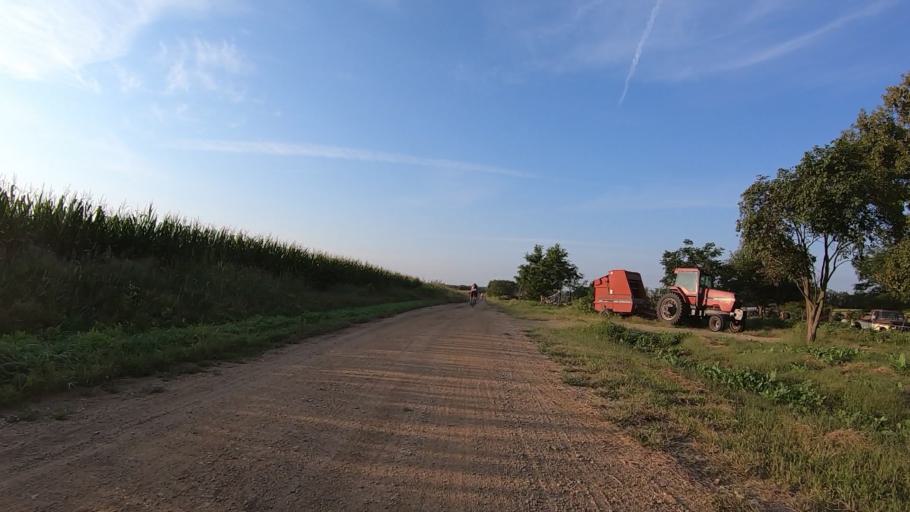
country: US
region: Kansas
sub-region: Marshall County
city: Blue Rapids
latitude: 39.7679
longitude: -96.7508
